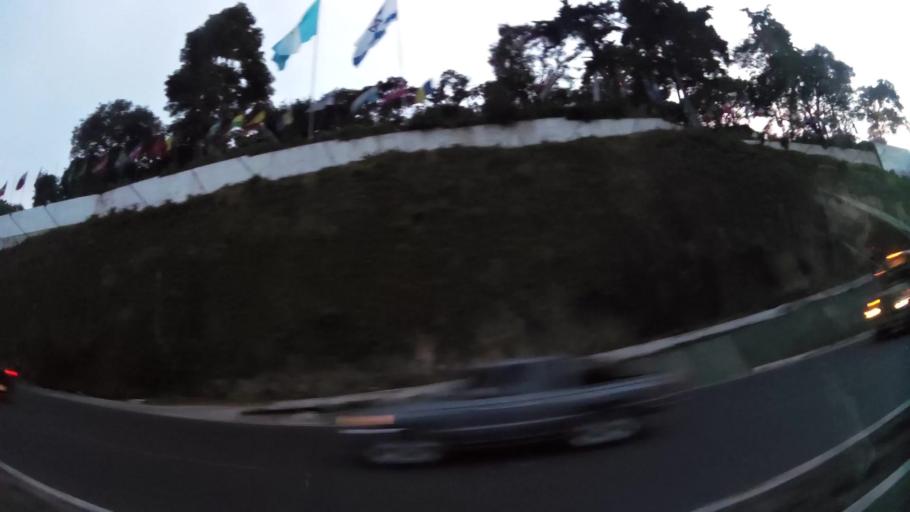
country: GT
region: Guatemala
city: Mixco
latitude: 14.6251
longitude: -90.6065
